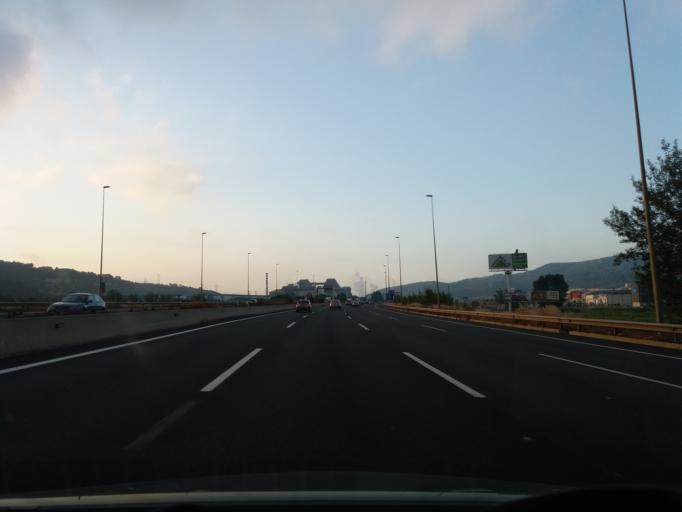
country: ES
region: Catalonia
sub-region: Provincia de Barcelona
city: Castellbisbal
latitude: 41.4629
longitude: 1.9719
